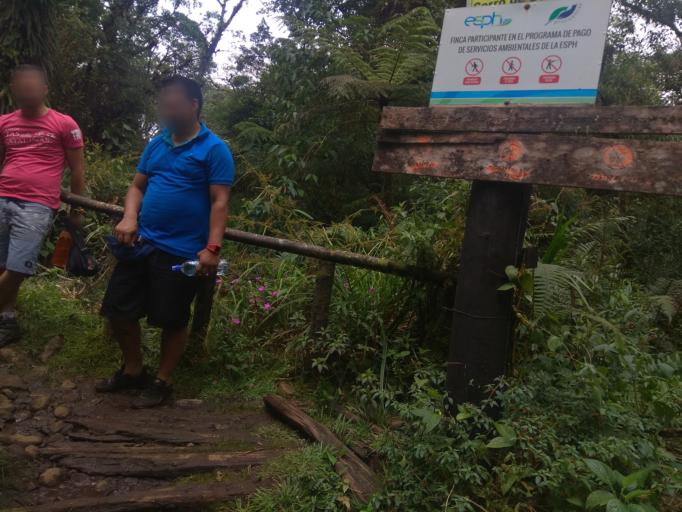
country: CR
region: Heredia
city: San Josecito
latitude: 10.0941
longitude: -84.0588
